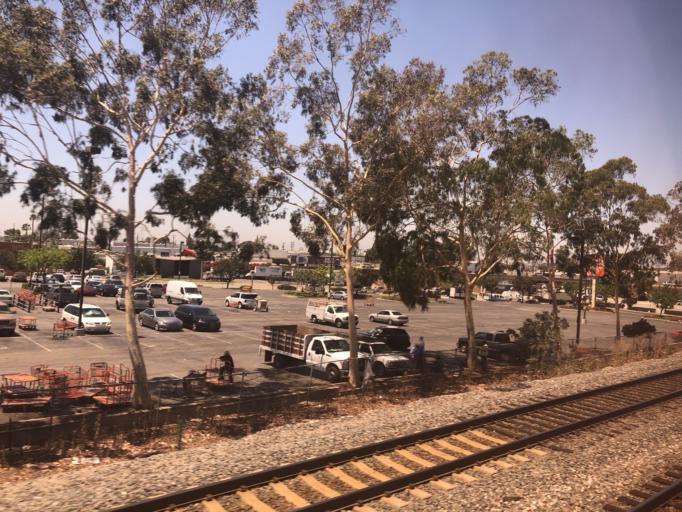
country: US
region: California
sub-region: Los Angeles County
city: Commerce
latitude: 33.9879
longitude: -118.1351
